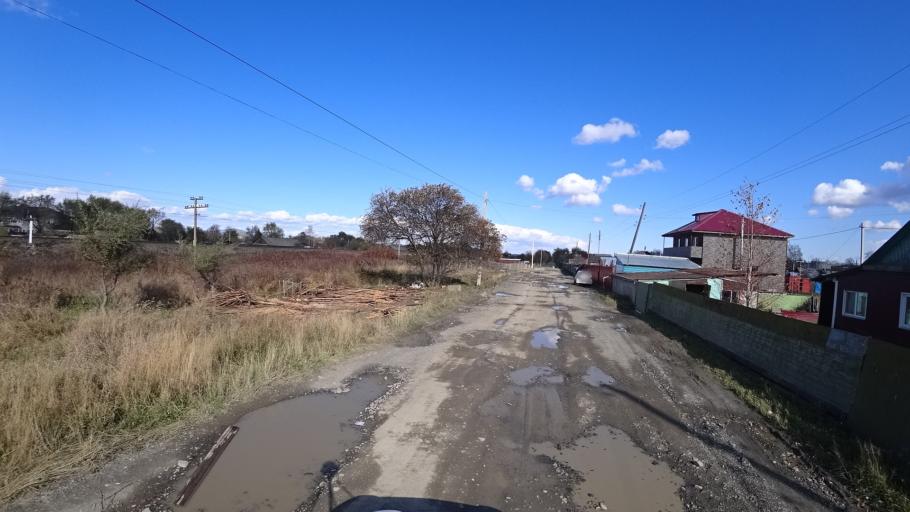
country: RU
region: Khabarovsk Krai
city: Amursk
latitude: 50.0939
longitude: 136.5032
